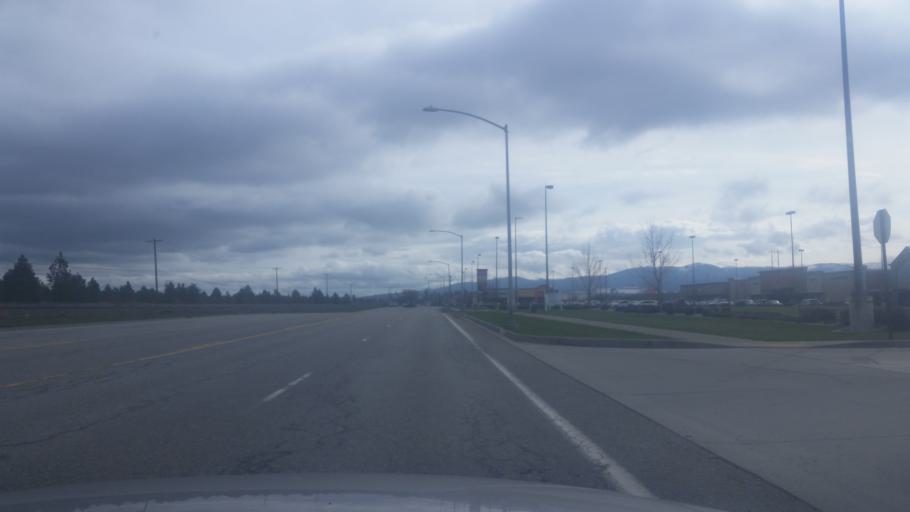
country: US
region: Washington
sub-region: Spokane County
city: Spokane Valley
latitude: 47.6758
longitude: -117.2186
